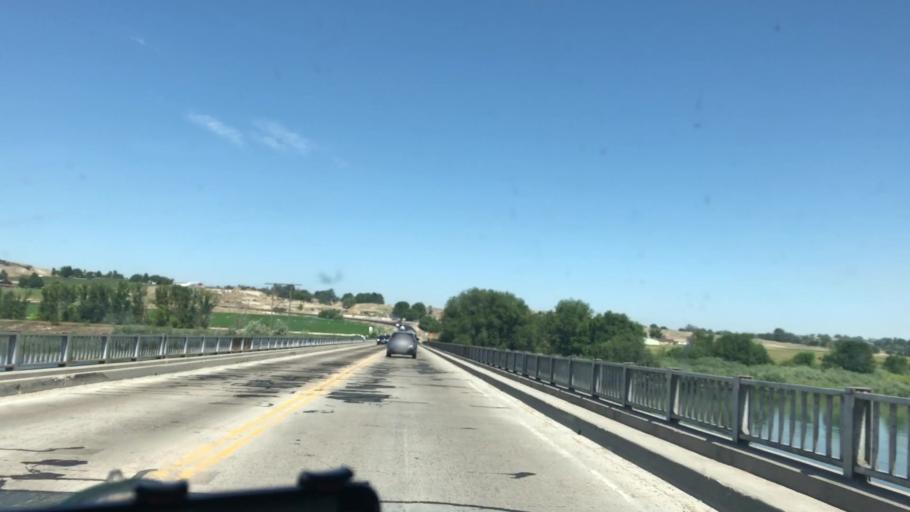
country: US
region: Idaho
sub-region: Owyhee County
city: Marsing
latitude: 43.5481
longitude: -116.8009
